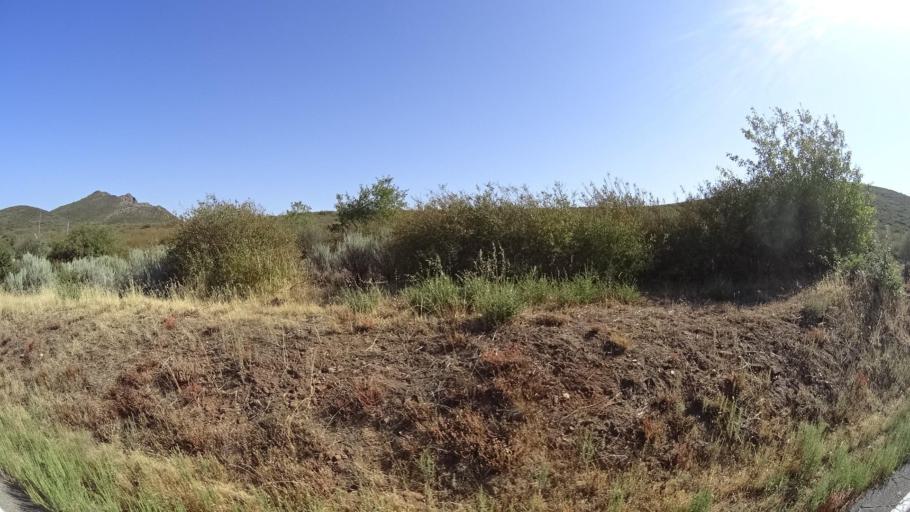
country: US
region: California
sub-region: San Diego County
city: Pine Valley
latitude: 32.9112
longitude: -116.4608
